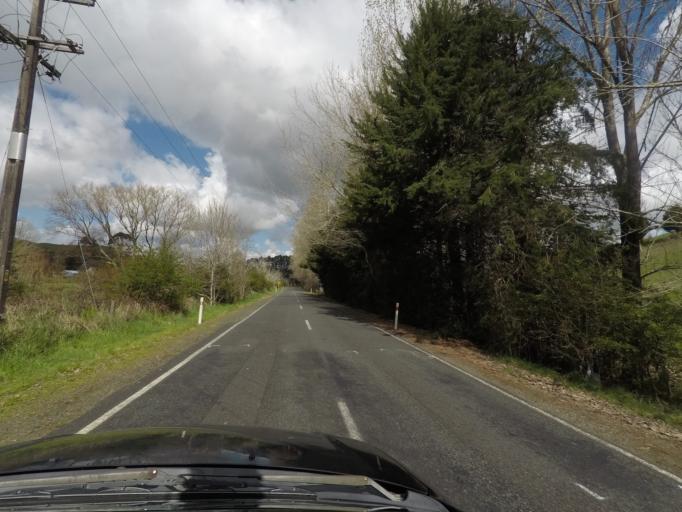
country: NZ
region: Auckland
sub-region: Auckland
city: Red Hill
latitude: -37.1093
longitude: 175.0999
